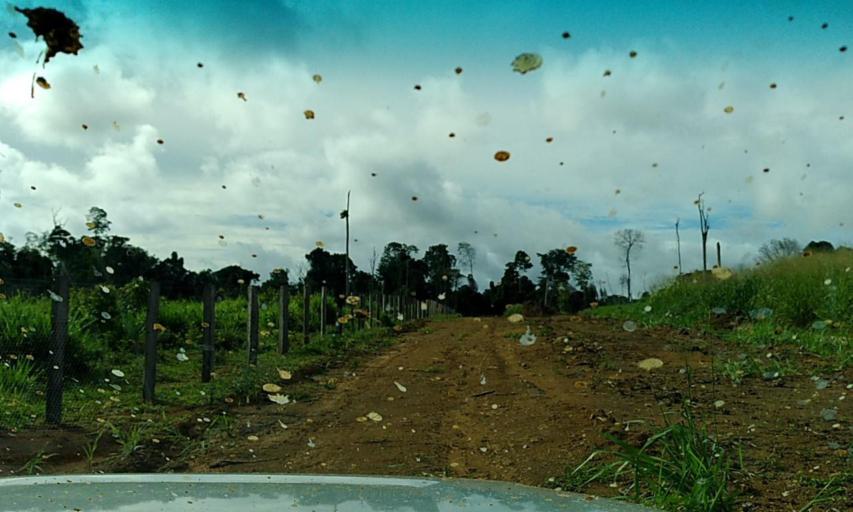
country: BR
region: Para
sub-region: Senador Jose Porfirio
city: Senador Jose Porfirio
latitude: -3.0001
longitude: -51.7407
